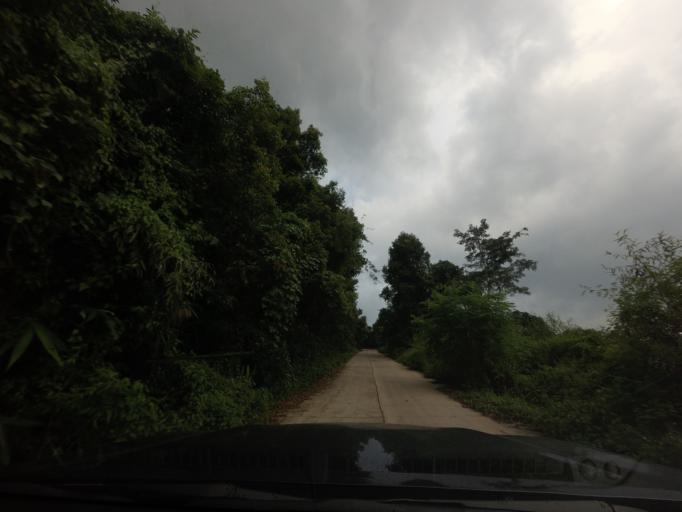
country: TH
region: Nan
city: Bo Kluea
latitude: 19.3502
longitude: 101.1636
